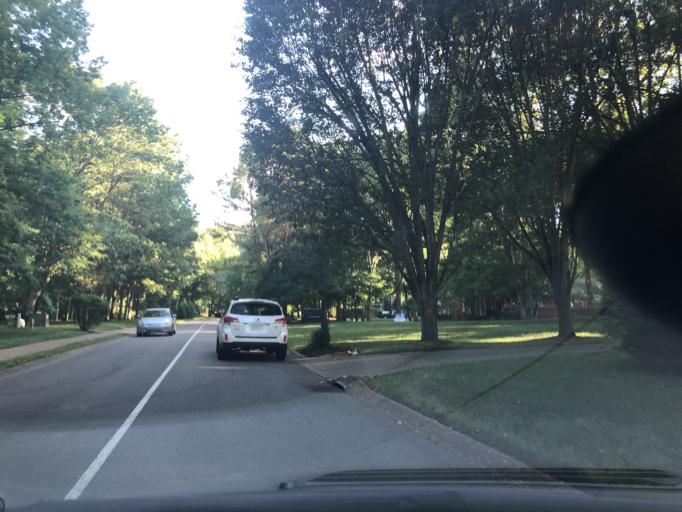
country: US
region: Tennessee
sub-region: Davidson County
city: Forest Hills
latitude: 36.0575
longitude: -86.8347
